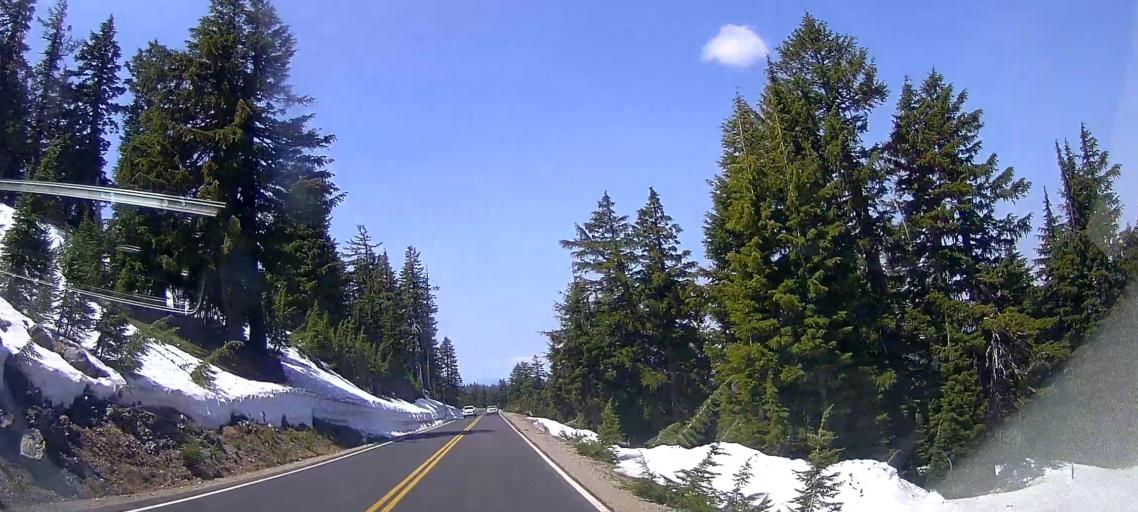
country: US
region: Oregon
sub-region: Jackson County
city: Shady Cove
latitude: 42.9722
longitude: -122.1461
